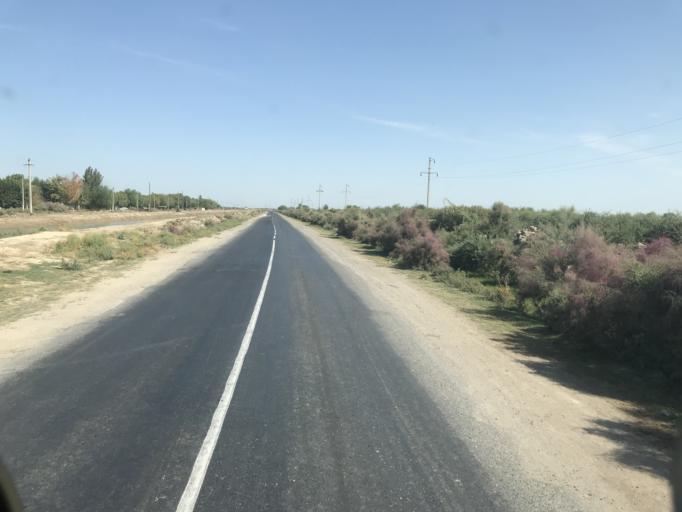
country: KZ
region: Ongtustik Qazaqstan
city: Myrzakent
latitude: 40.7170
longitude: 68.5345
